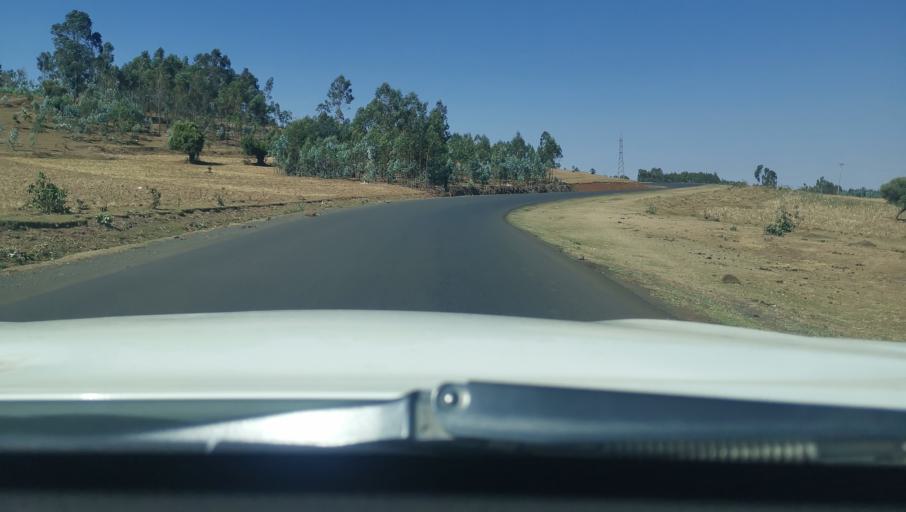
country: ET
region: Oromiya
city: Gedo
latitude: 8.9790
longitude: 37.4735
